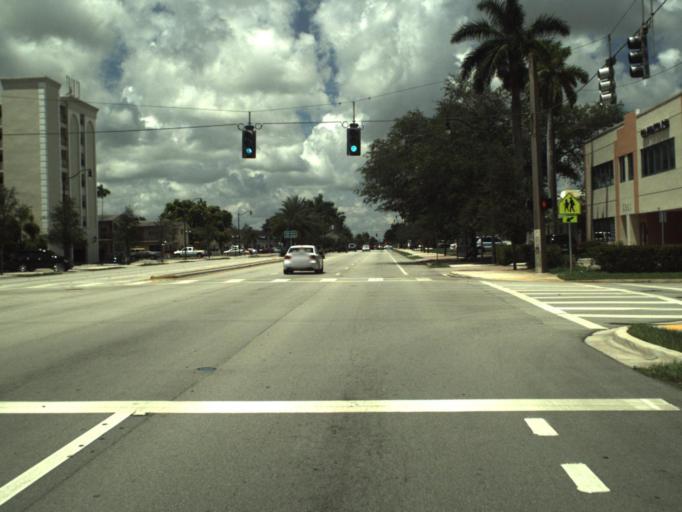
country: US
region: Florida
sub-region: Broward County
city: Carver Ranches
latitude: 26.0104
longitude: -80.1955
